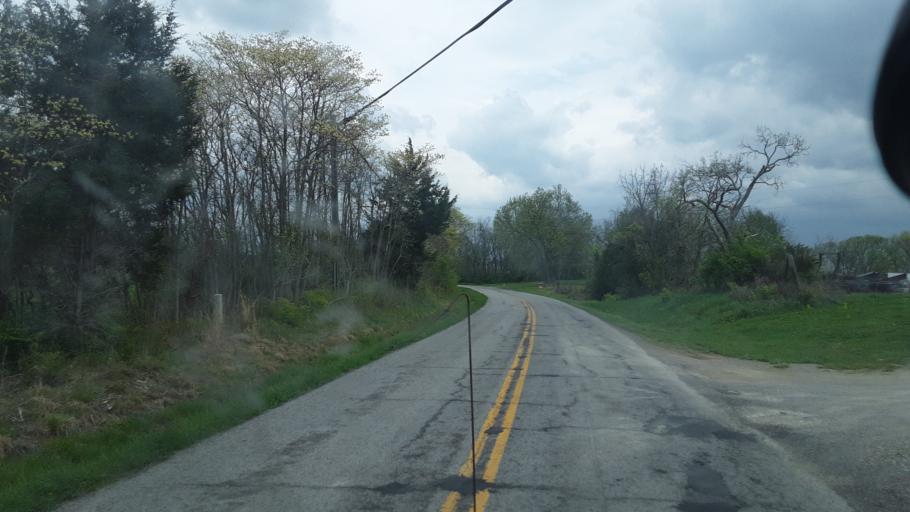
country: US
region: Kentucky
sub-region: Grant County
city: Dry Ridge
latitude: 38.6569
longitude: -84.6902
